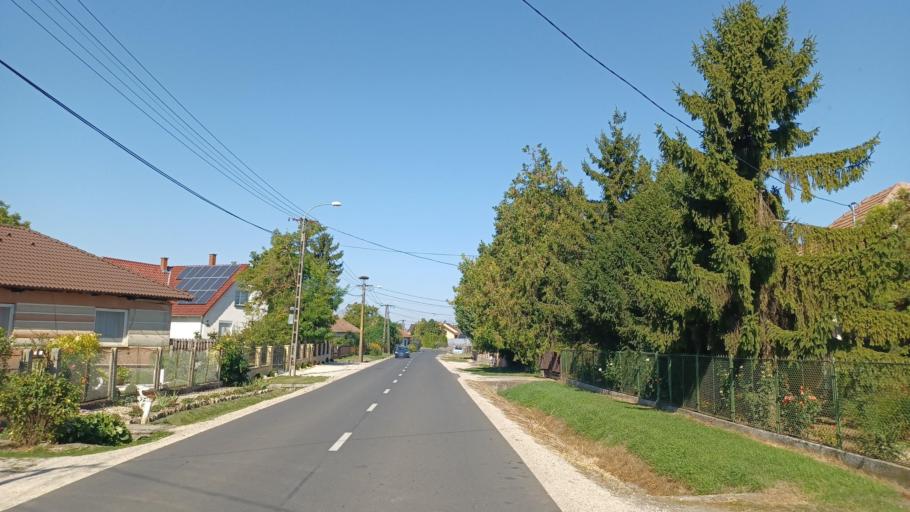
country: HU
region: Fejer
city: Cece
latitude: 46.7669
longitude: 18.6382
